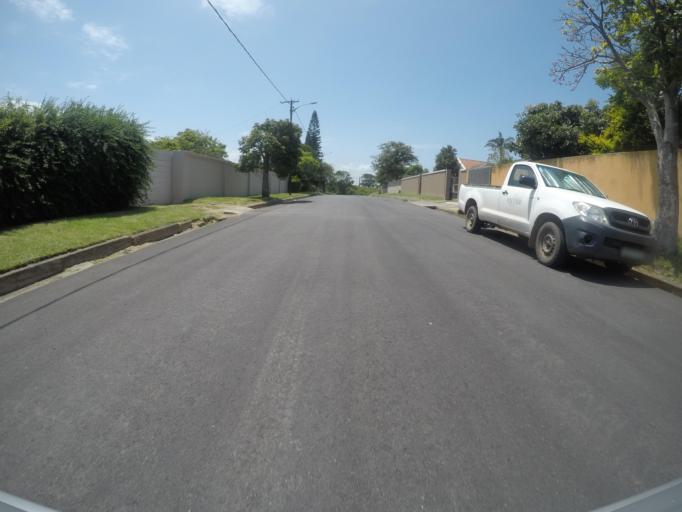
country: ZA
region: Eastern Cape
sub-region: Buffalo City Metropolitan Municipality
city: East London
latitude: -32.9729
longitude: 27.8793
